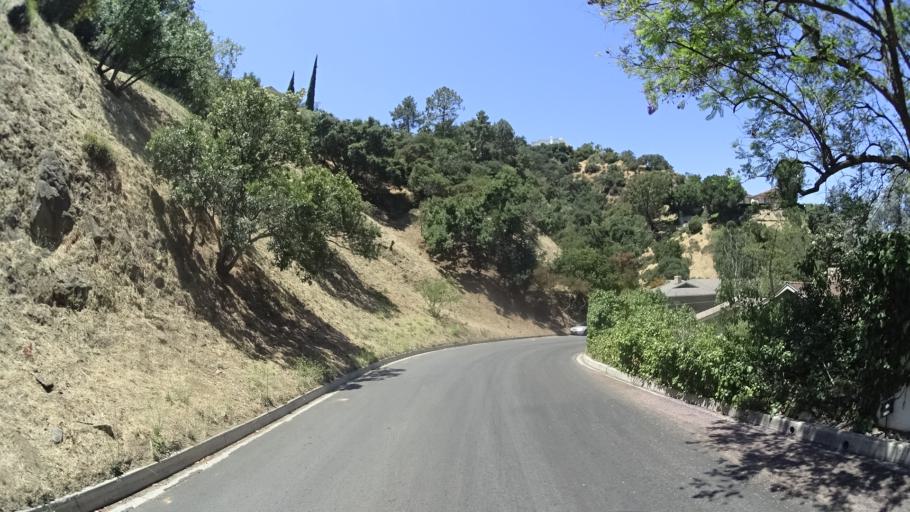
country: US
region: California
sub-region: Los Angeles County
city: Universal City
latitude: 34.1331
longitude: -118.3700
